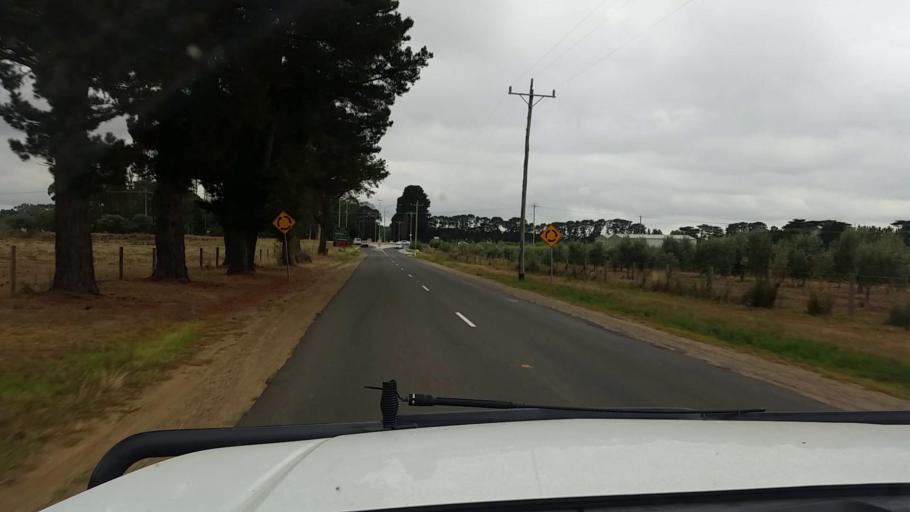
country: AU
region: Victoria
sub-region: Mornington Peninsula
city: Hastings
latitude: -38.3025
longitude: 145.1456
